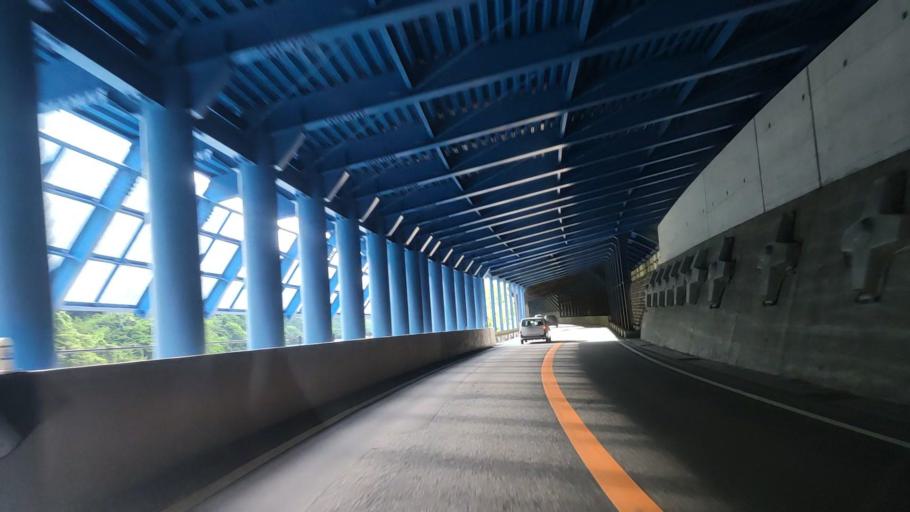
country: JP
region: Toyama
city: Yatsuomachi-higashikumisaka
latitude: 36.4175
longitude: 137.2887
